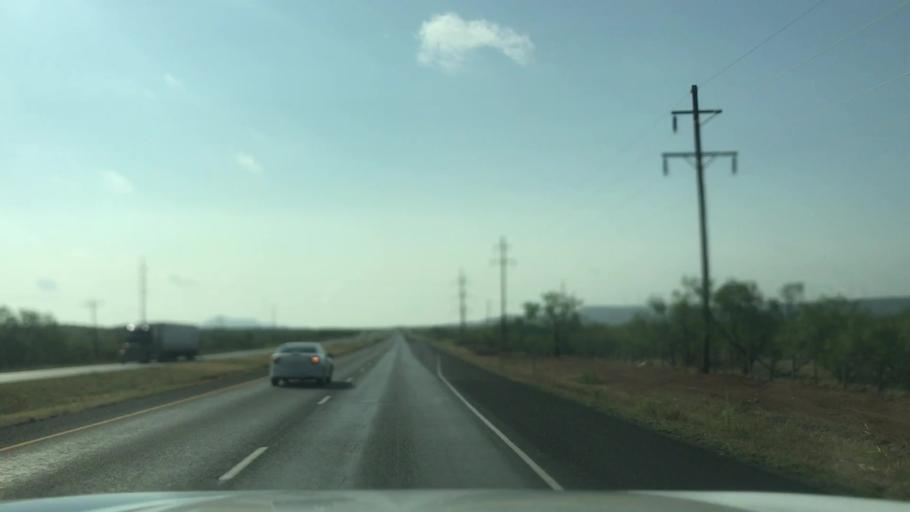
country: US
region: Texas
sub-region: Garza County
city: Post
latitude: 32.9972
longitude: -101.1534
